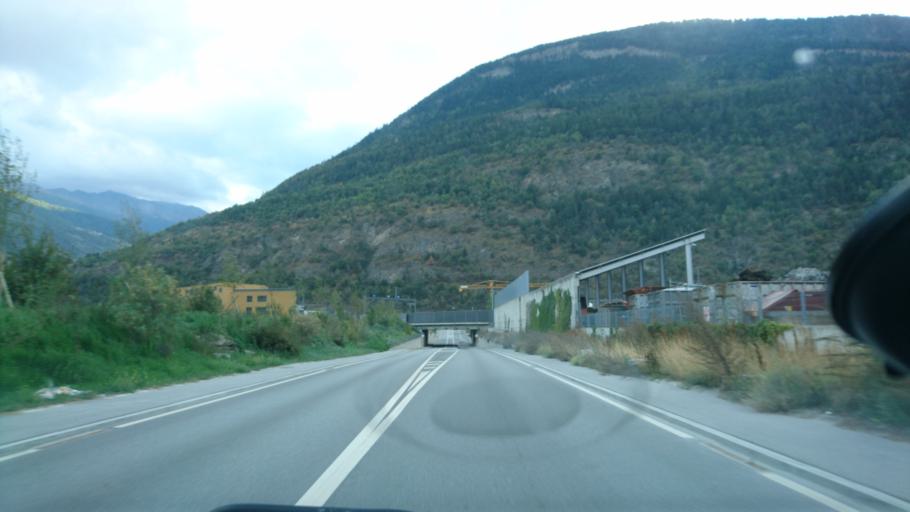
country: CH
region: Valais
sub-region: Visp District
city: Baltschieder
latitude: 46.2999
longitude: 7.8664
